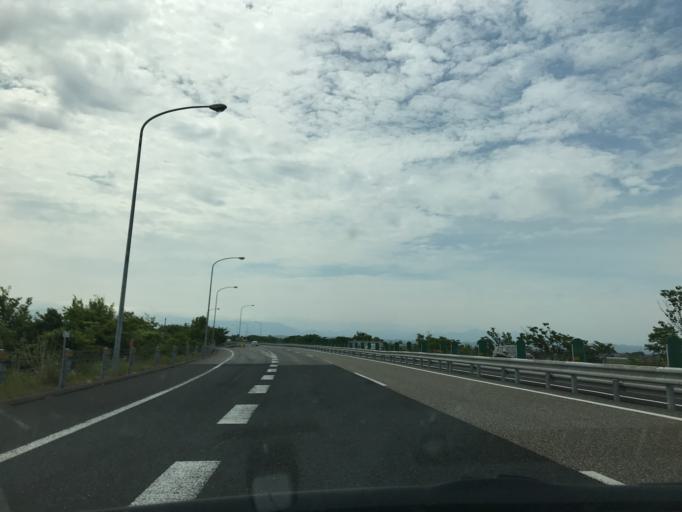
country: JP
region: Niigata
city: Kameda-honcho
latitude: 37.8514
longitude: 139.0558
